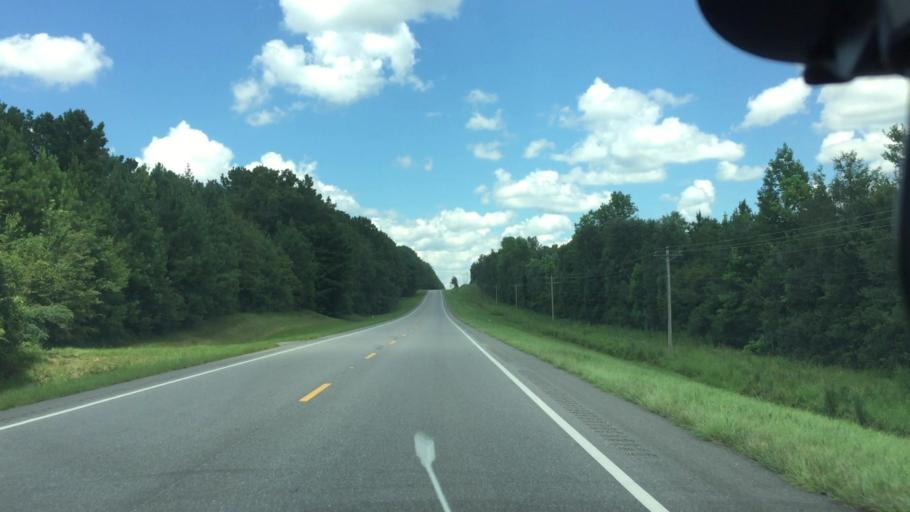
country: US
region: Alabama
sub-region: Coffee County
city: New Brockton
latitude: 31.5103
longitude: -85.9163
